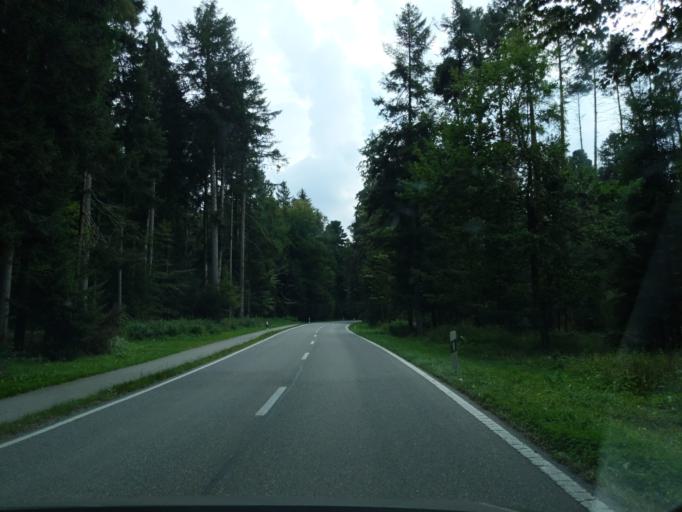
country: CH
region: Bern
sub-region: Oberaargau
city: Wyssachen
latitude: 47.1021
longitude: 7.8272
